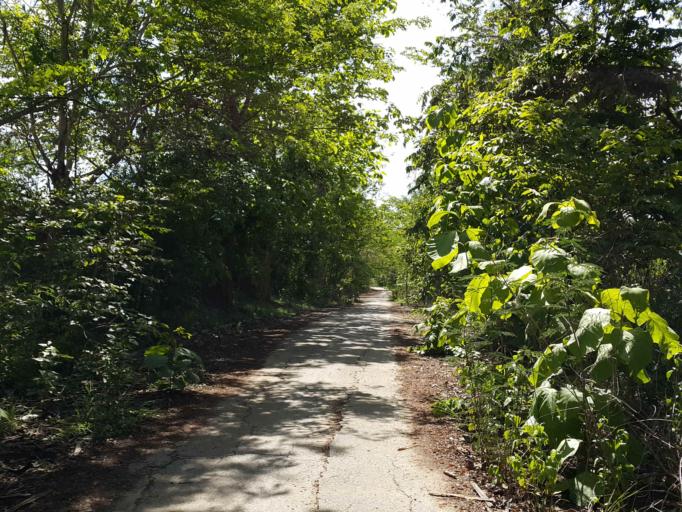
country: TH
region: Chiang Mai
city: San Kamphaeng
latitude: 18.7560
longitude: 99.1173
